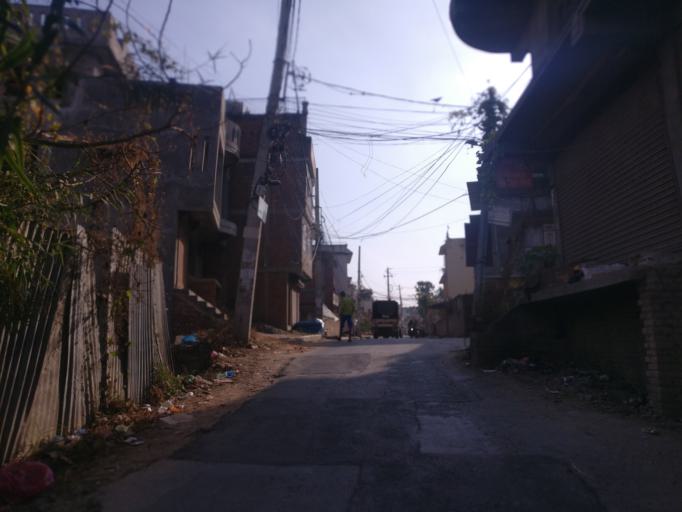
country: NP
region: Central Region
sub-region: Bagmati Zone
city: Patan
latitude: 27.6837
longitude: 85.3260
